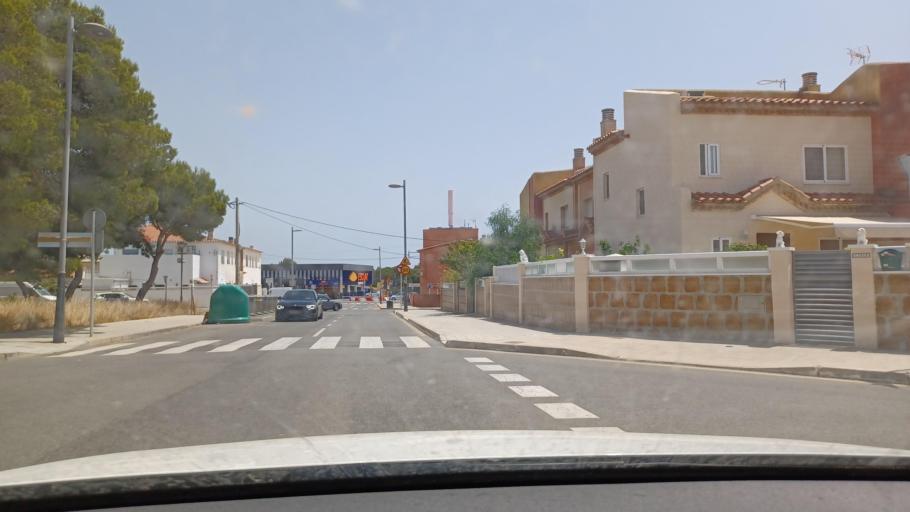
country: ES
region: Catalonia
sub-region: Provincia de Tarragona
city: Colldejou
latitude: 41.0012
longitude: 0.9286
